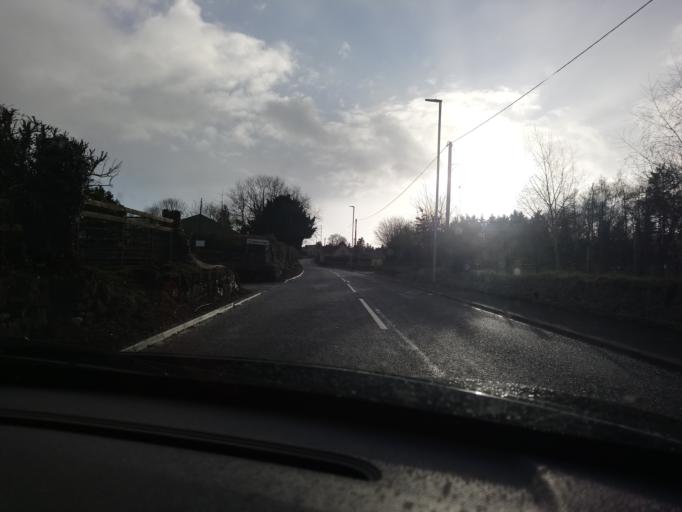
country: GB
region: Wales
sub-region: Wrexham
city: Chirk
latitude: 52.9637
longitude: -3.0577
